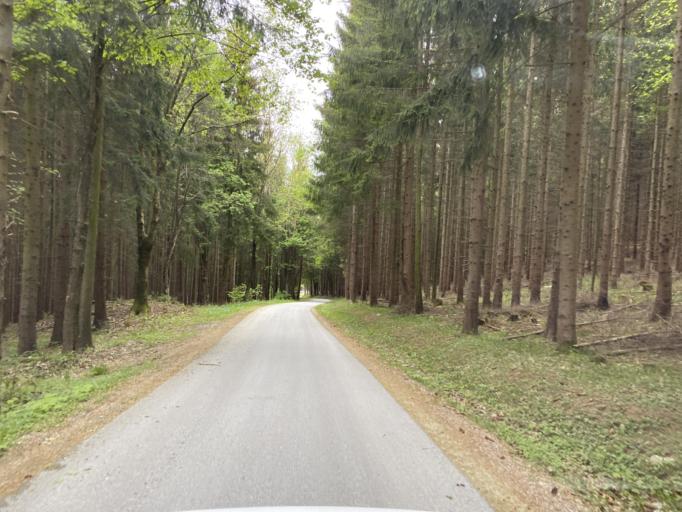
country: AT
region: Styria
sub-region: Politischer Bezirk Weiz
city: Baierdorf-Umgebung
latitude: 47.3099
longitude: 15.7103
